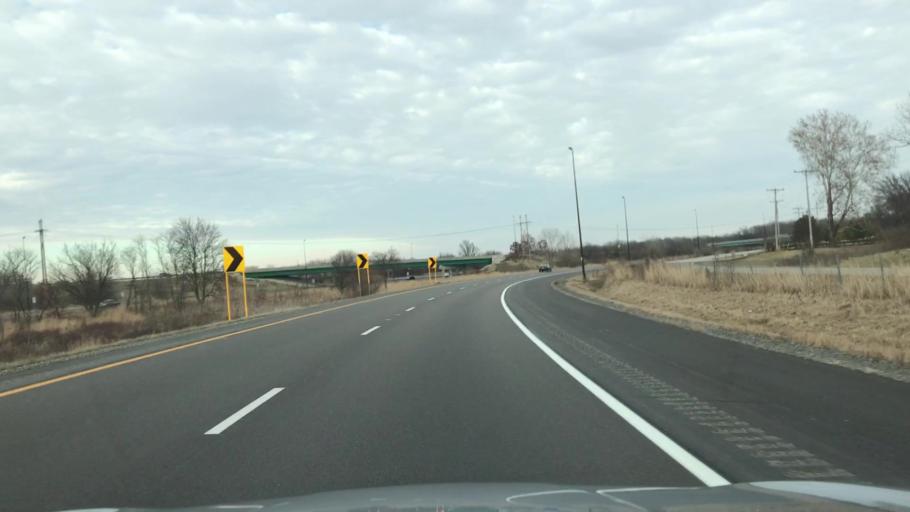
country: US
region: Illinois
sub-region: Sangamon County
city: Southern View
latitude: 39.7402
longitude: -89.6417
